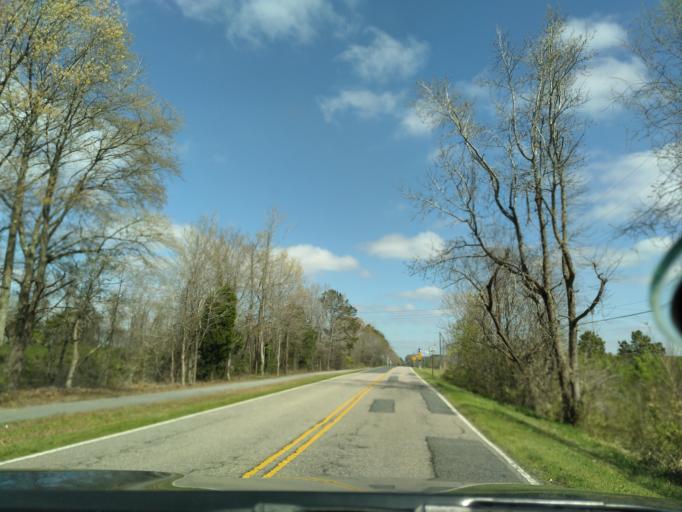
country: US
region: Virginia
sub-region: City of Portsmouth
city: Portsmouth Heights
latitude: 36.7183
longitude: -76.3511
